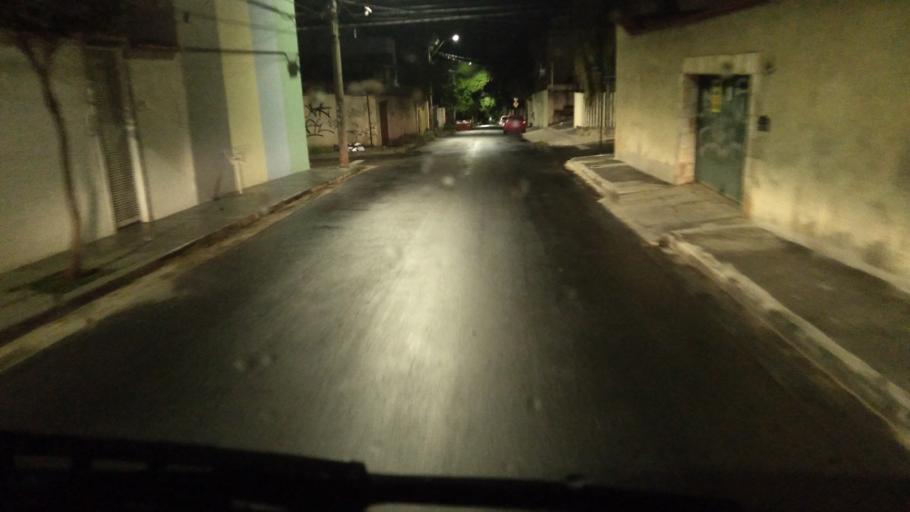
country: BR
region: Minas Gerais
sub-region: Belo Horizonte
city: Belo Horizonte
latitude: -19.8984
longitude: -43.9180
